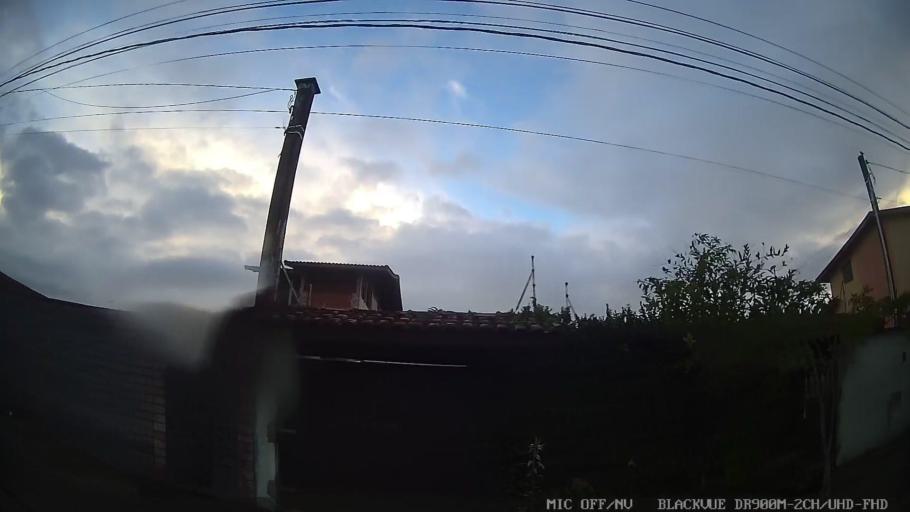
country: BR
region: Sao Paulo
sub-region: Itanhaem
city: Itanhaem
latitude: -24.2001
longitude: -46.8324
